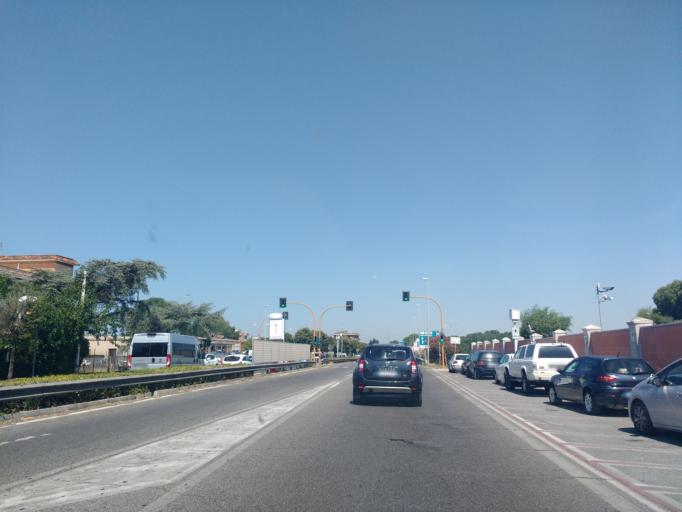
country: IT
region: Latium
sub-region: Citta metropolitana di Roma Capitale
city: Fiumicino-Isola Sacra
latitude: 41.7655
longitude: 12.2639
